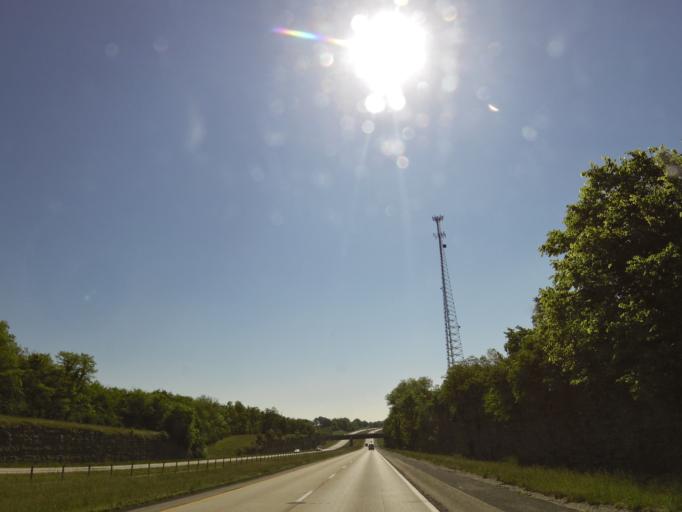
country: US
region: Kentucky
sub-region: Franklin County
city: Frankfort
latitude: 38.1733
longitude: -84.7935
